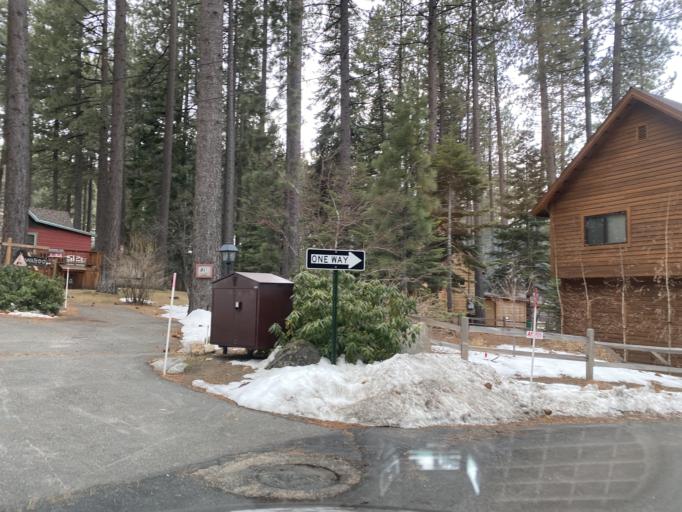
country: US
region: Nevada
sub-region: Douglas County
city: Kingsbury
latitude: 39.0036
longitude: -119.9484
